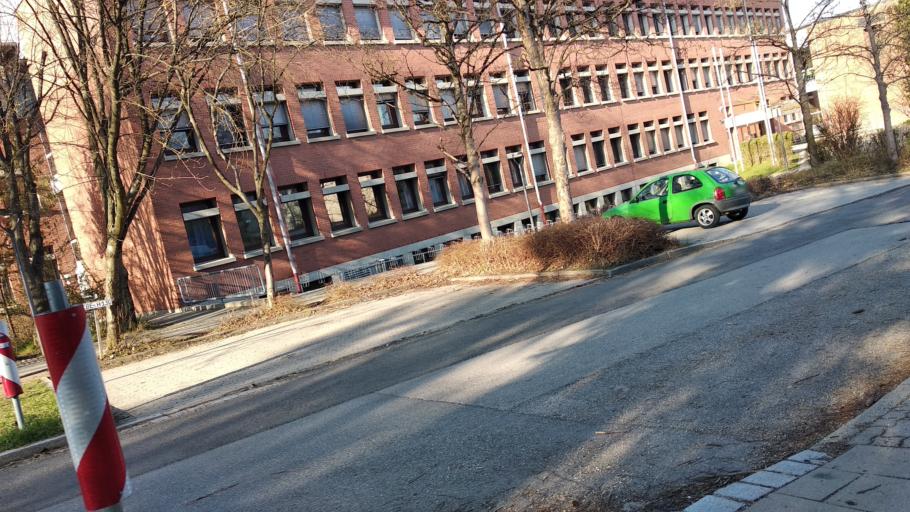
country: DE
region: Bavaria
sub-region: Upper Bavaria
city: Markt Schwaben
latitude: 48.1879
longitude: 11.8641
